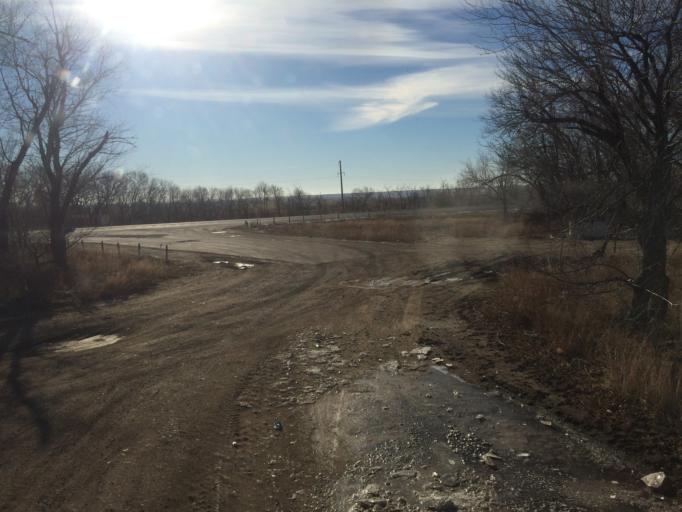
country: KZ
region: Aqtoebe
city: Aqtobe
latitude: 50.2481
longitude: 56.7891
